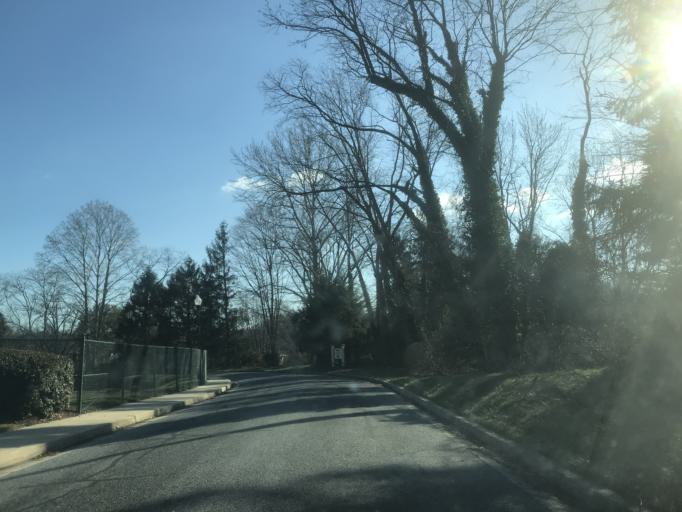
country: US
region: Maryland
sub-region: Baltimore County
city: Hampton
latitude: 39.4038
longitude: -76.5769
